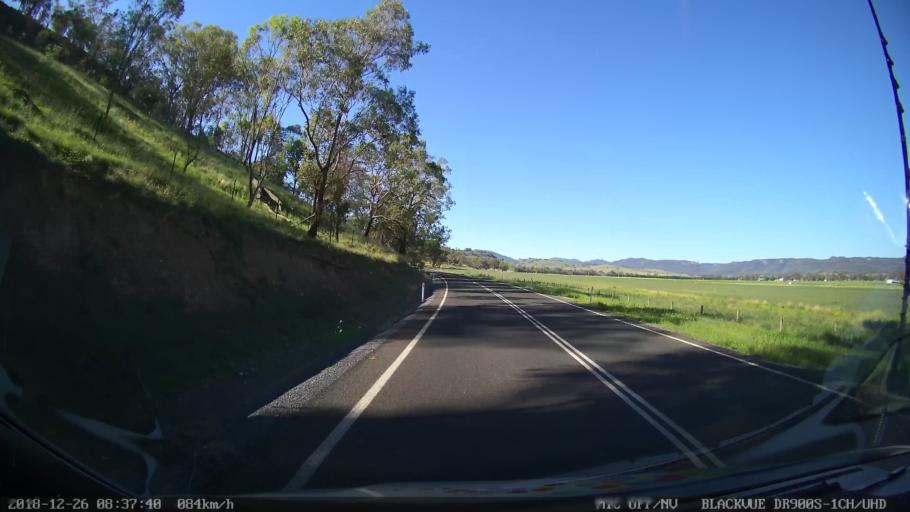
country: AU
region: New South Wales
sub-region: Upper Hunter Shire
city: Merriwa
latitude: -32.4345
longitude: 150.0878
